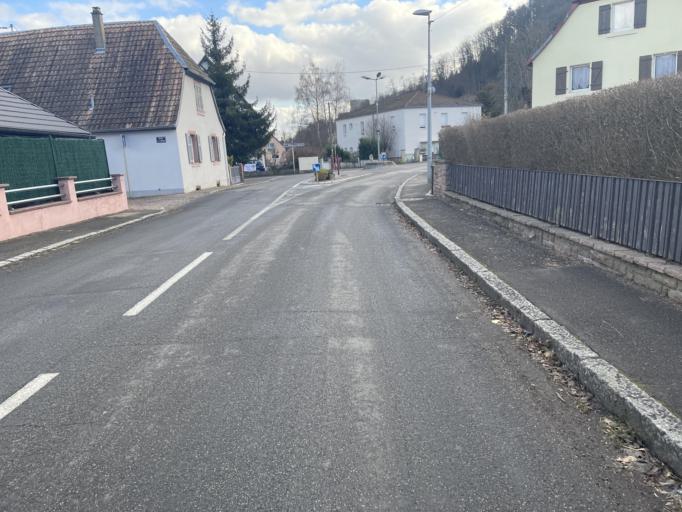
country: FR
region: Alsace
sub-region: Departement du Haut-Rhin
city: Buhl
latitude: 47.9254
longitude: 7.1873
